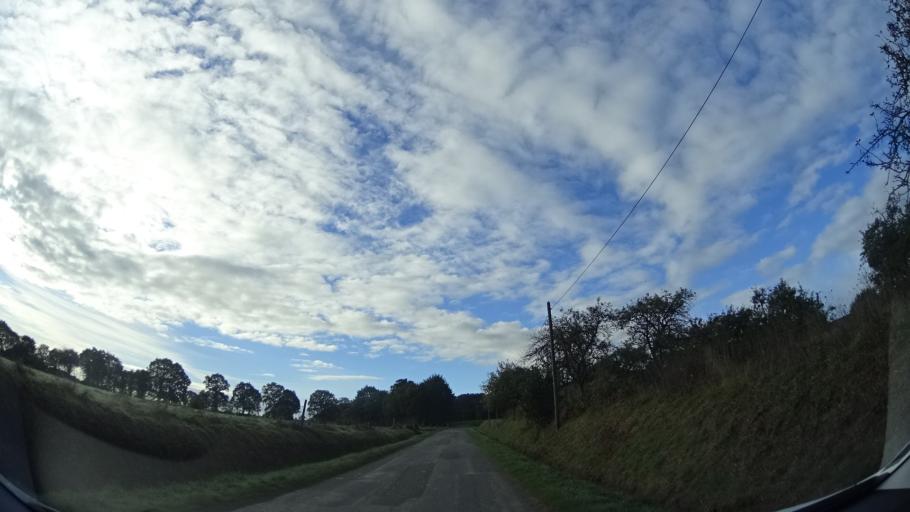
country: FR
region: Brittany
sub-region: Departement d'Ille-et-Vilaine
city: Geveze
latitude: 48.2106
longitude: -1.7999
